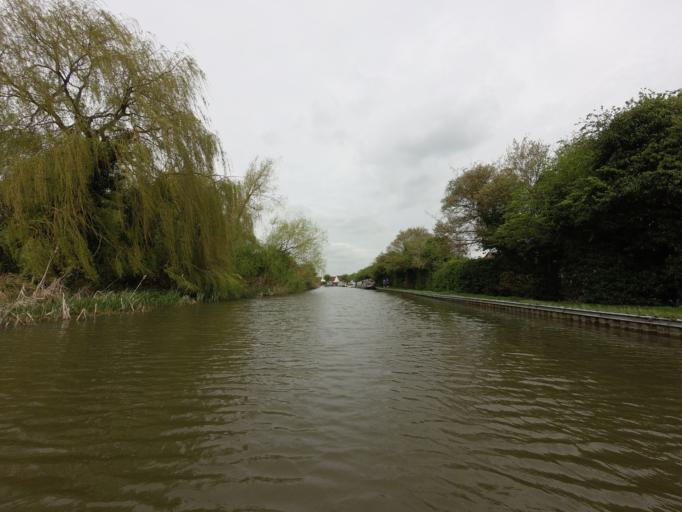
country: GB
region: England
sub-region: Milton Keynes
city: Newport Pagnell
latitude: 52.0703
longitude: -0.7460
